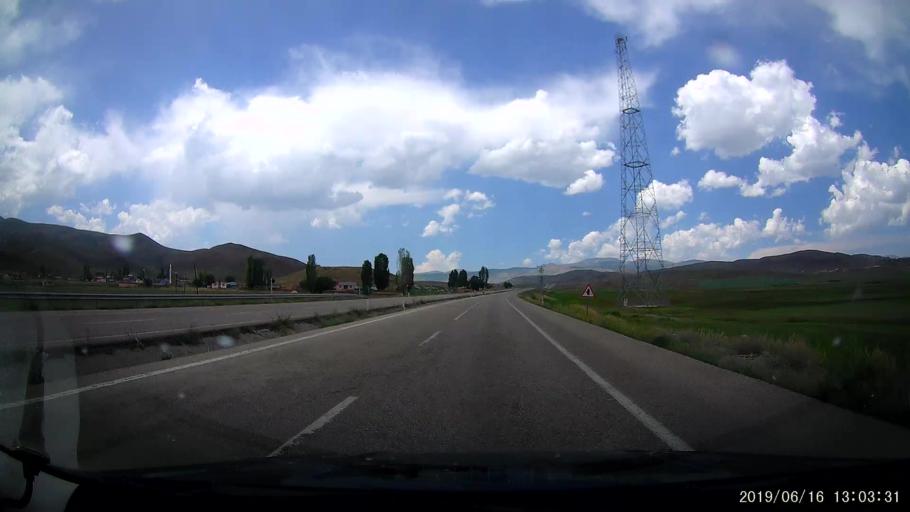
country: TR
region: Agri
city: Sulucem
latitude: 39.5822
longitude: 43.7886
